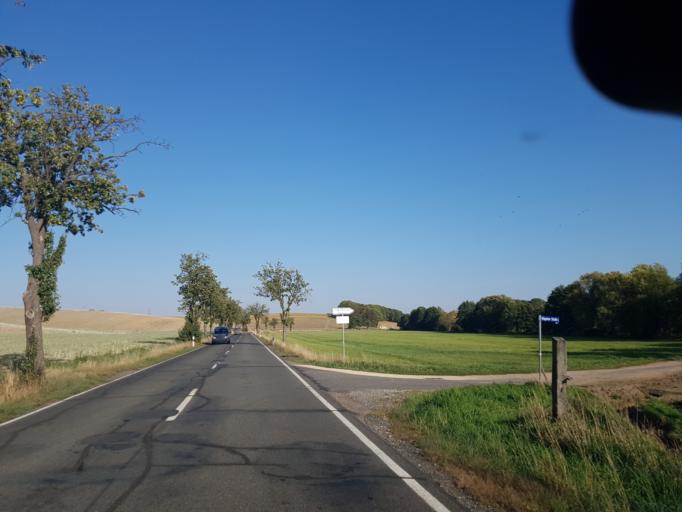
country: DE
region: Saxony
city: Ostrau
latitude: 51.1968
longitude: 13.1287
